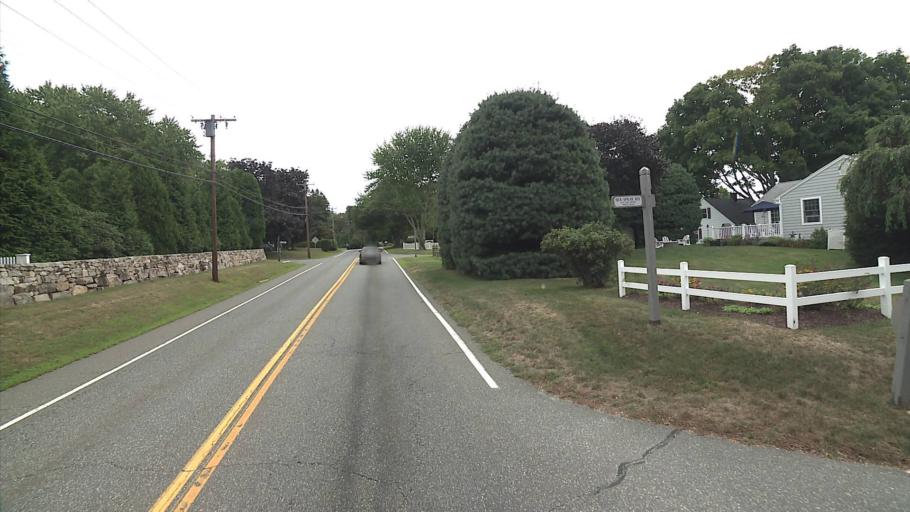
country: US
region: Connecticut
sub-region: New London County
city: Niantic
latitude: 41.2901
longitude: -72.2740
